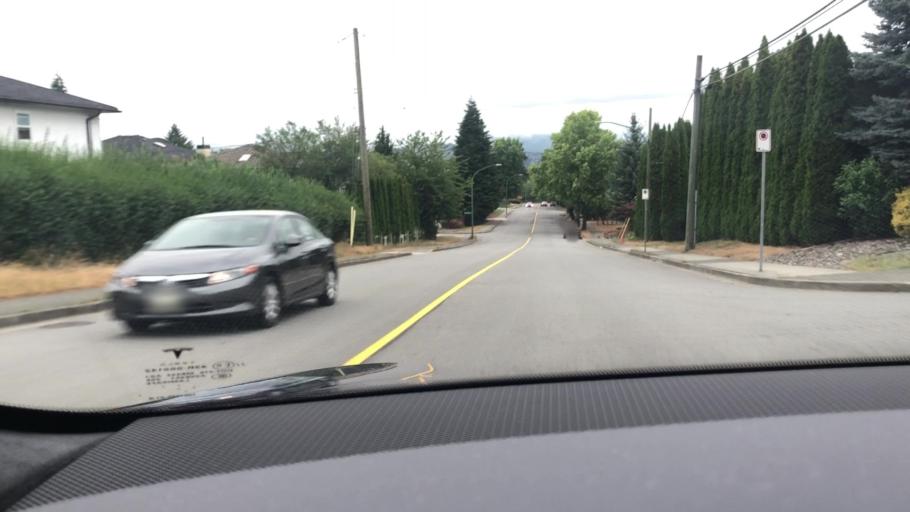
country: CA
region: British Columbia
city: Burnaby
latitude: 49.2259
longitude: -122.9720
